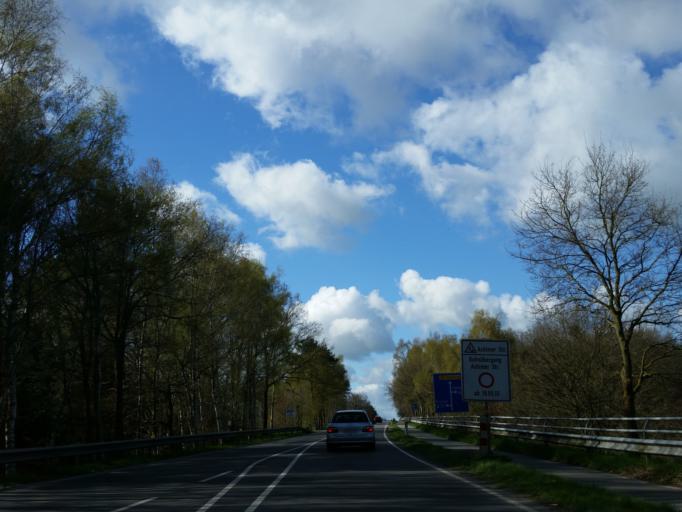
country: DE
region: Lower Saxony
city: Verden
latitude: 52.9624
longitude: 9.2479
